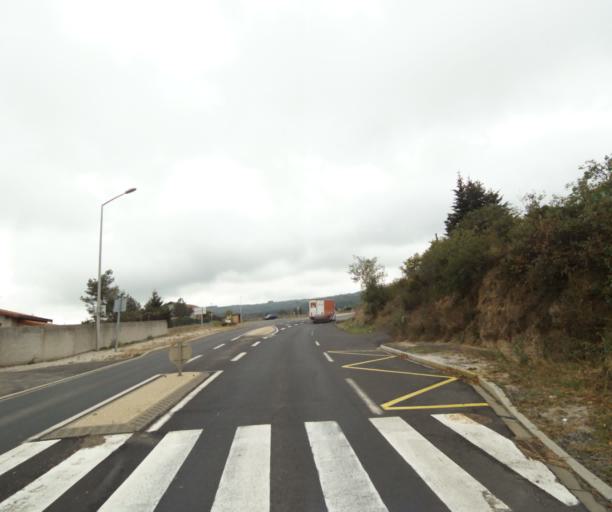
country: FR
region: Auvergne
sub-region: Departement du Puy-de-Dome
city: Ceyrat
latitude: 45.7067
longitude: 3.0538
